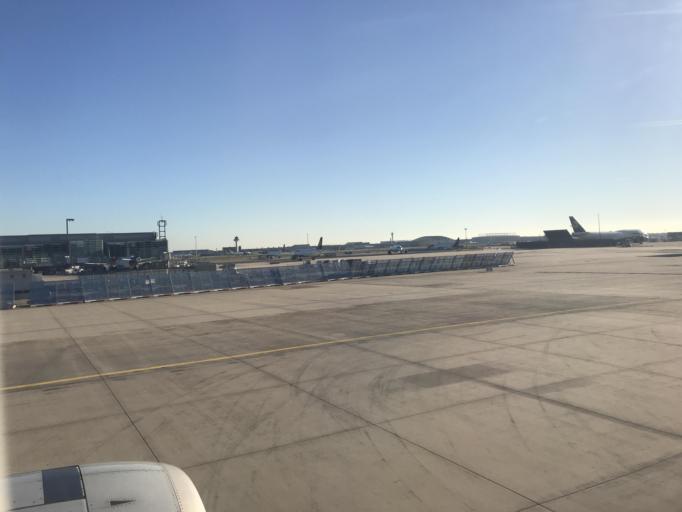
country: DE
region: Hesse
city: Kelsterbach
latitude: 50.0461
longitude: 8.5610
